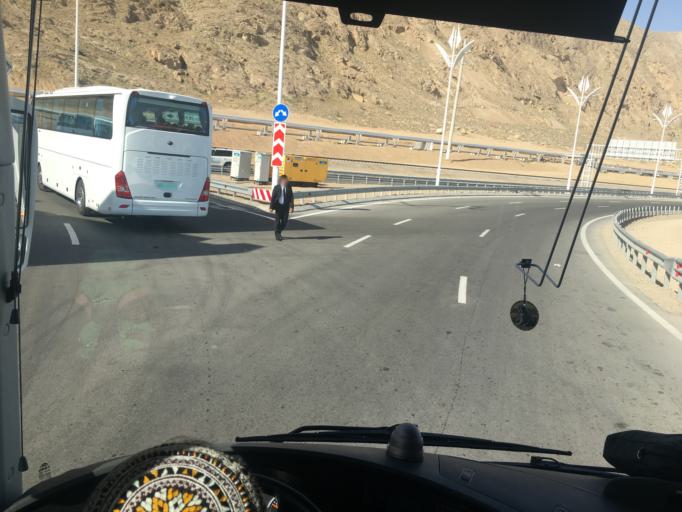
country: TM
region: Balkan
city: Turkmenbasy
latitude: 40.0078
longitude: 53.0242
